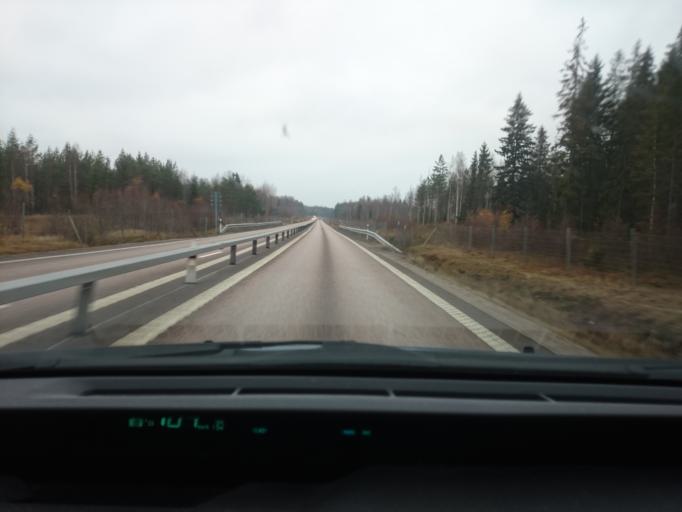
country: SE
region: Dalarna
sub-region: Avesta Kommun
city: Avesta
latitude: 60.0987
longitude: 16.3134
